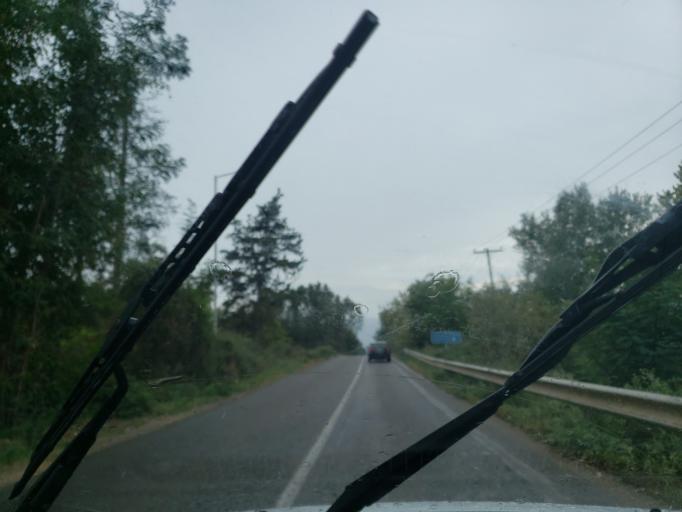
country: GR
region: Central Greece
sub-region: Nomos Fthiotidos
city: Anthili
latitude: 38.8504
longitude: 22.4405
